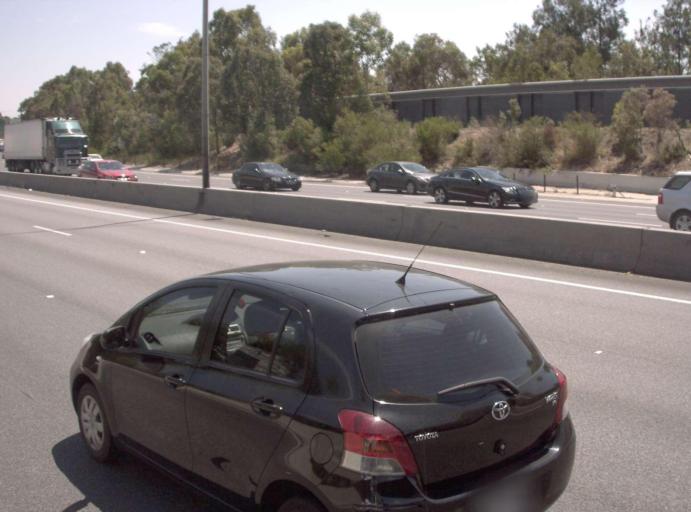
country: AU
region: Victoria
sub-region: Stonnington
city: Glen Iris
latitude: -37.8672
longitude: 145.0617
